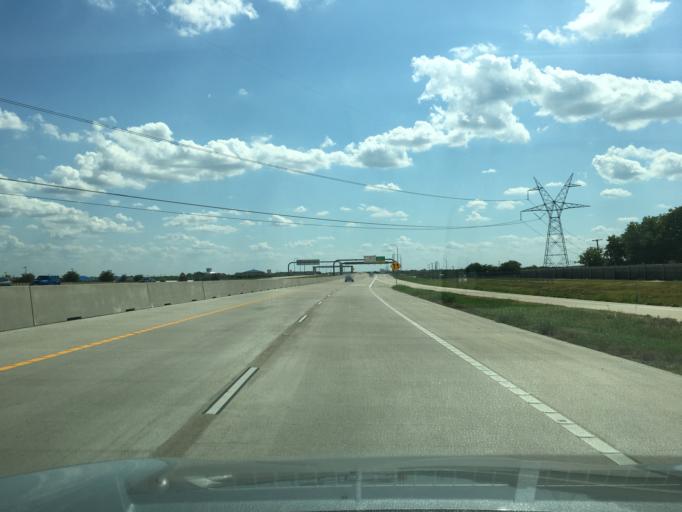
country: US
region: Texas
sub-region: Tarrant County
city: Mansfield
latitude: 32.6310
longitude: -97.0666
